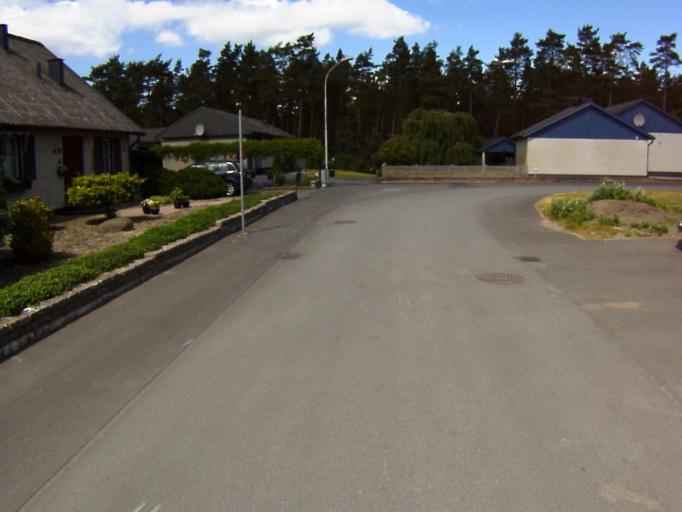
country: SE
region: Skane
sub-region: Kristianstads Kommun
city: Ahus
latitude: 55.9477
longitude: 14.2724
